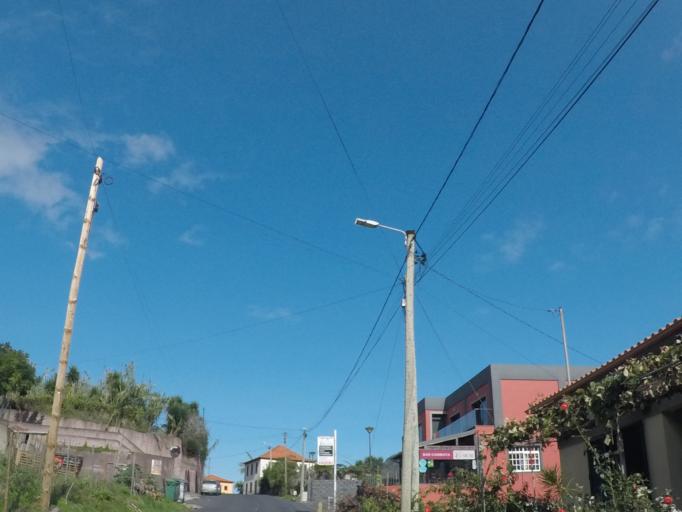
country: PT
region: Madeira
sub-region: Sao Vicente
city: Sao Vicente
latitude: 32.7862
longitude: -17.0337
